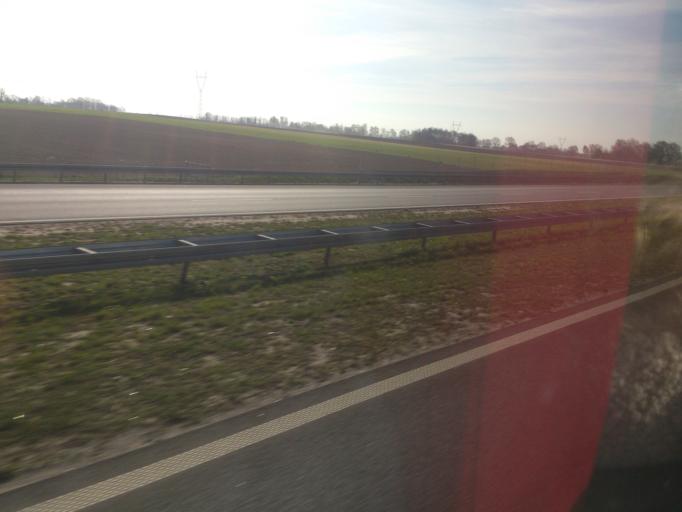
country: PL
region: Kujawsko-Pomorskie
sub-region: Powiat aleksandrowski
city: Waganiec
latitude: 52.7783
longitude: 18.8440
